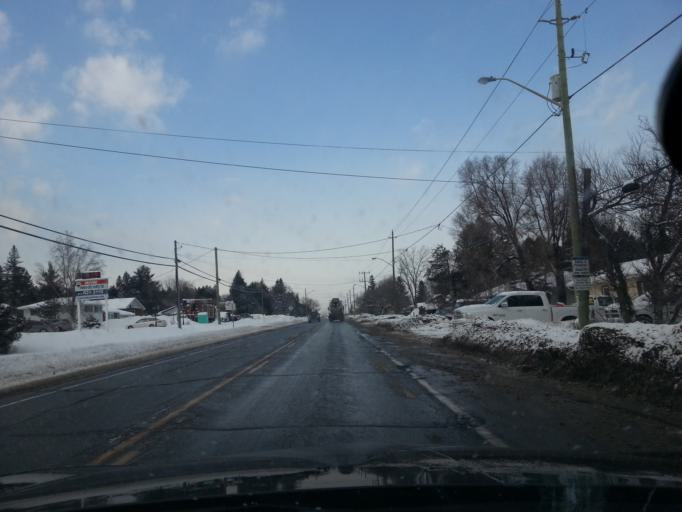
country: CA
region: Ontario
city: Bells Corners
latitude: 45.2728
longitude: -75.9465
